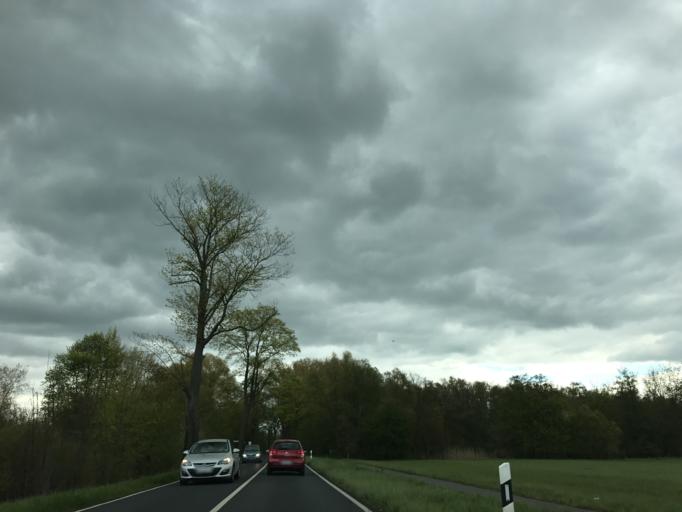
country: DE
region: Brandenburg
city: Ketzin
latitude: 52.4855
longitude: 12.8338
